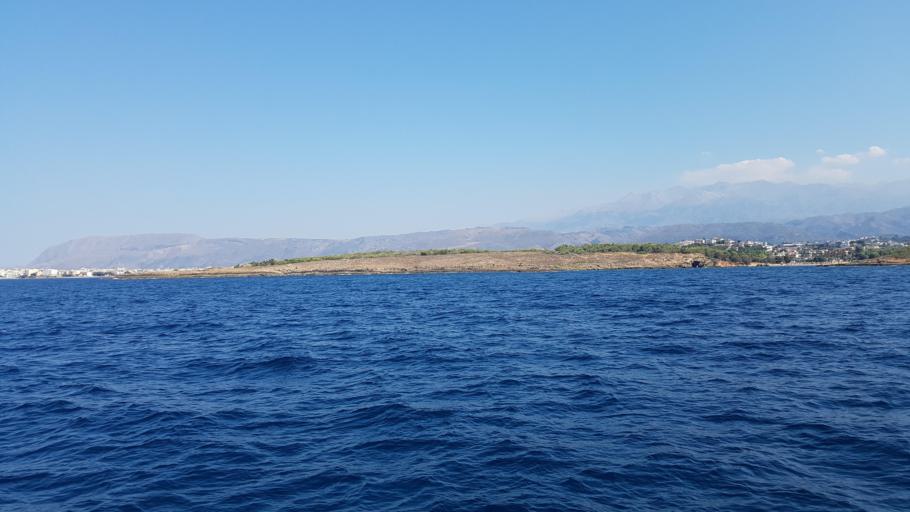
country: GR
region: Crete
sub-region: Nomos Chanias
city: Daratsos
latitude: 35.5217
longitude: 23.9824
